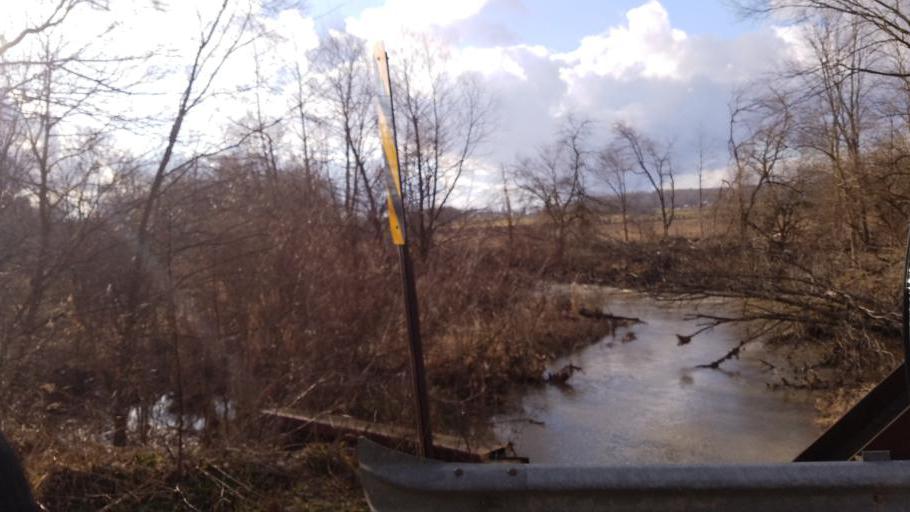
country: US
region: Ohio
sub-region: Knox County
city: Fredericktown
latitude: 40.5446
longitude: -82.6200
